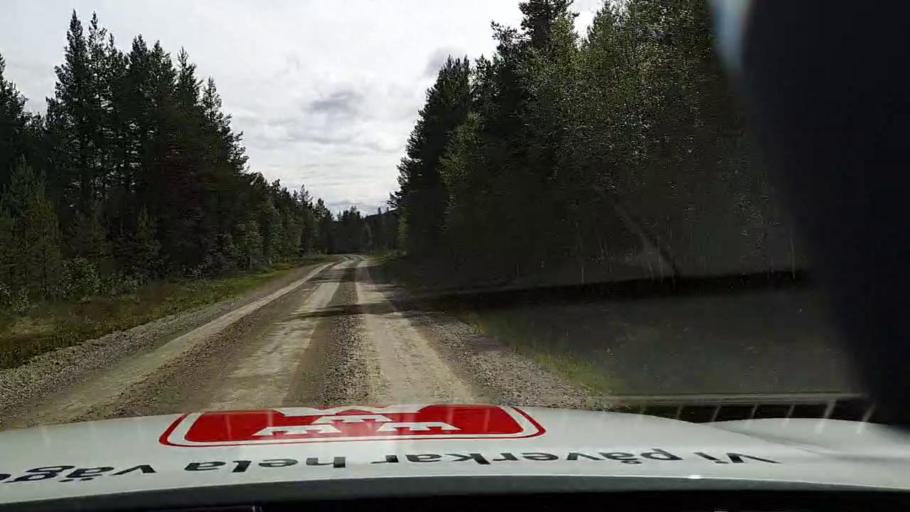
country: SE
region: Jaemtland
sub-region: Are Kommun
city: Jarpen
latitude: 62.5010
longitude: 13.5017
